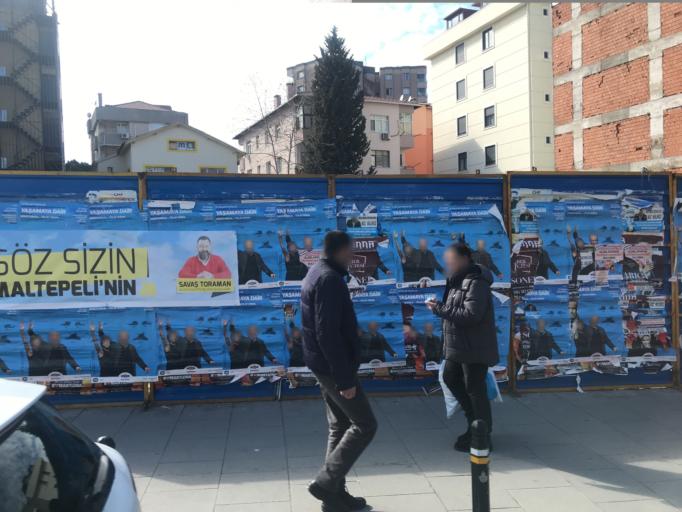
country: TR
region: Istanbul
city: Maltepe
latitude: 40.9267
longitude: 29.1296
